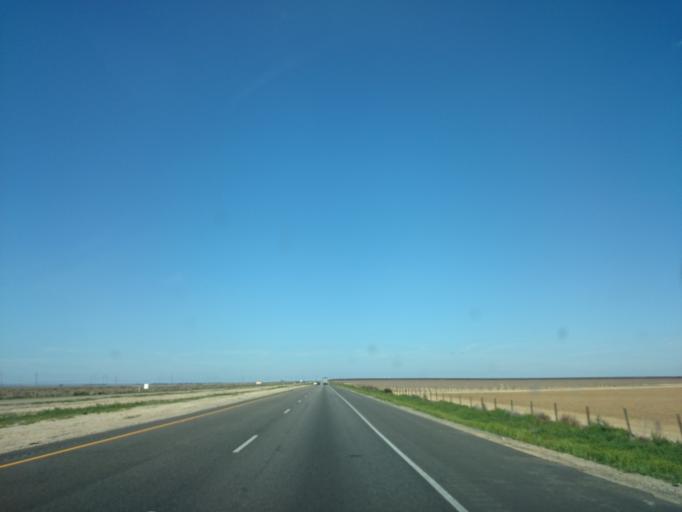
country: US
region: California
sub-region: Kern County
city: Buttonwillow
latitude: 35.4677
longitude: -119.4915
